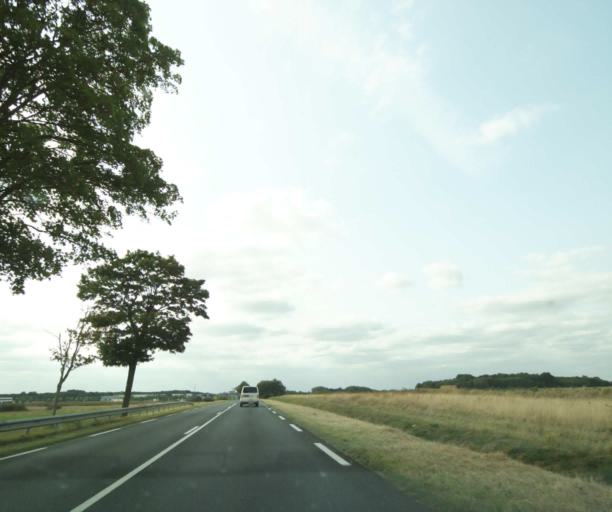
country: FR
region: Centre
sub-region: Departement d'Indre-et-Loire
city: Truyes
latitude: 47.2508
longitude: 0.8503
